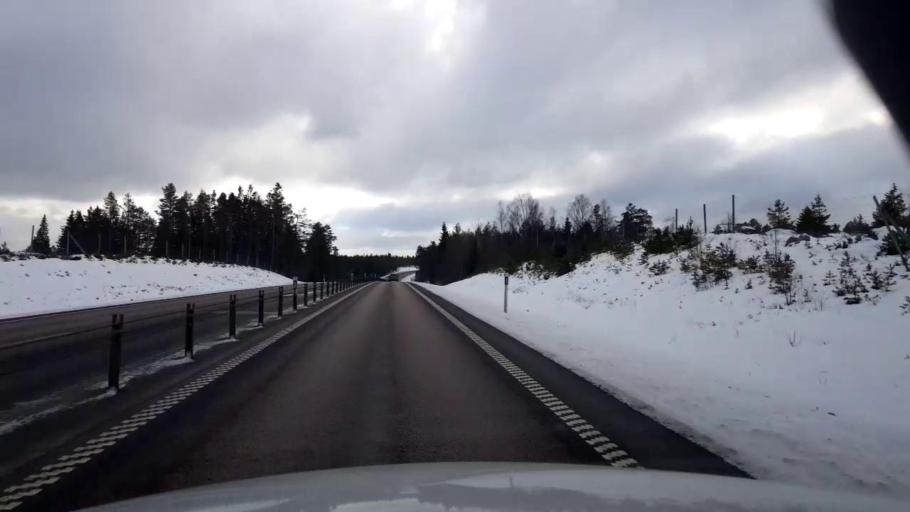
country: SE
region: Gaevleborg
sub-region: Hudiksvalls Kommun
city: Hudiksvall
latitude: 61.8173
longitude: 17.1899
